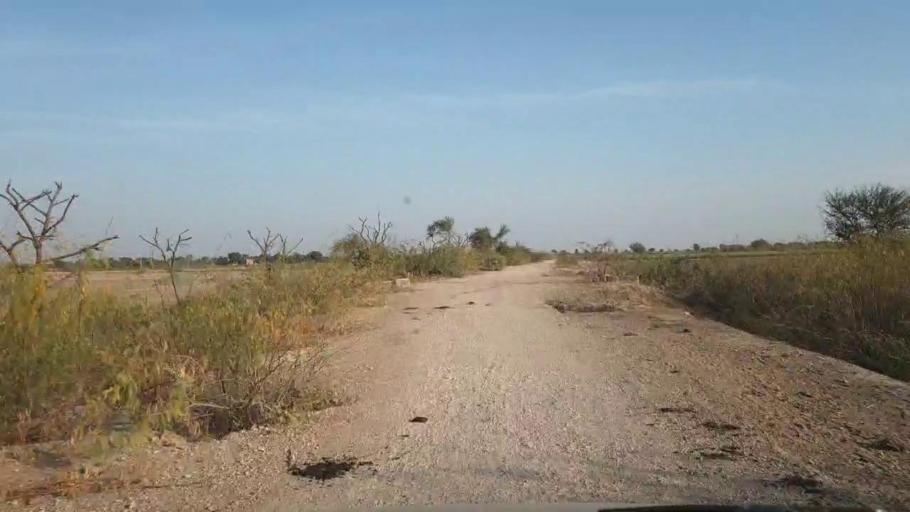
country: PK
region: Sindh
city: Chambar
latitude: 25.2409
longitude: 68.7972
